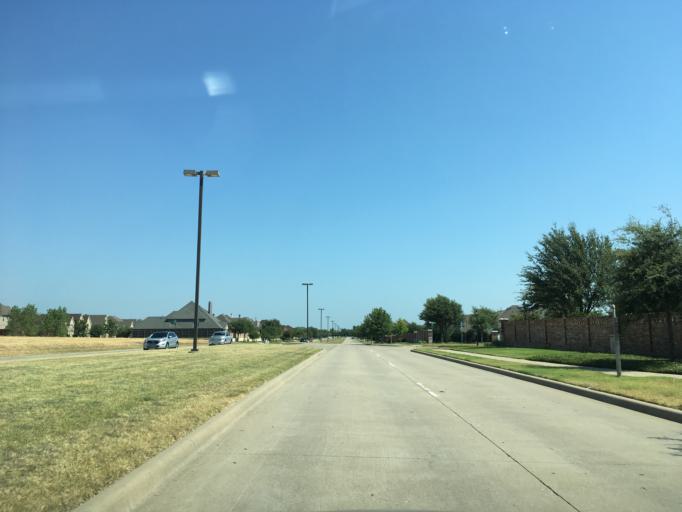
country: US
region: Texas
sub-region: Collin County
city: Allen
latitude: 33.1318
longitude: -96.6763
